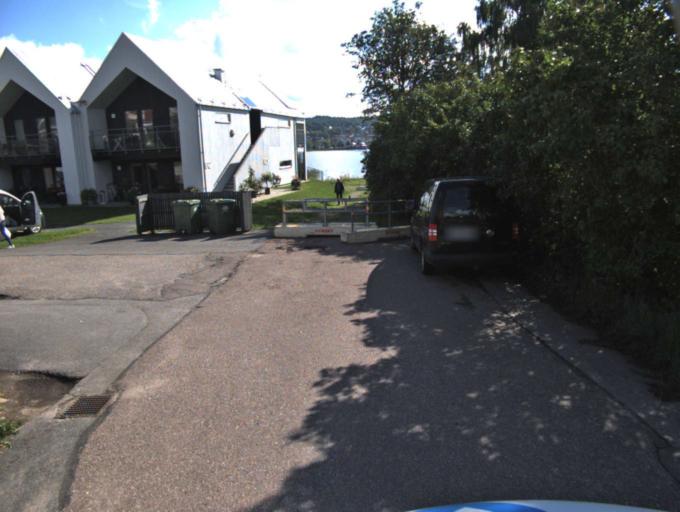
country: SE
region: Vaestra Goetaland
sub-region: Ulricehamns Kommun
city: Ulricehamn
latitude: 57.7989
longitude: 13.3962
